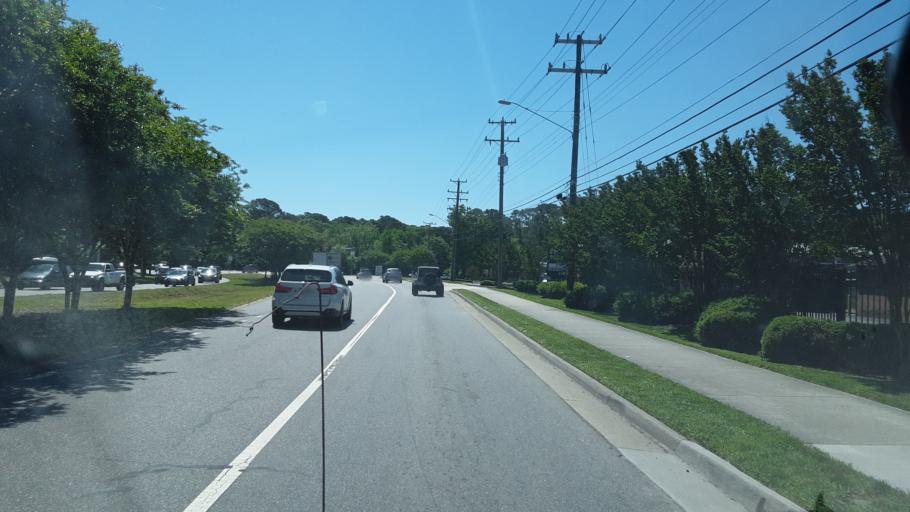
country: US
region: Virginia
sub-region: City of Virginia Beach
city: Virginia Beach
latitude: 36.7944
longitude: -75.9989
